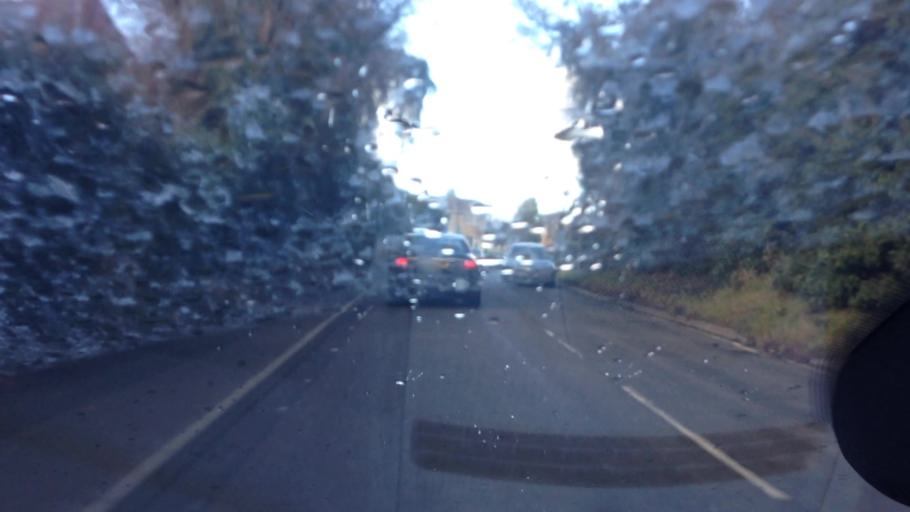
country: GB
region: England
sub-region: North Yorkshire
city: Knaresborough
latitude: 54.0009
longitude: -1.4502
